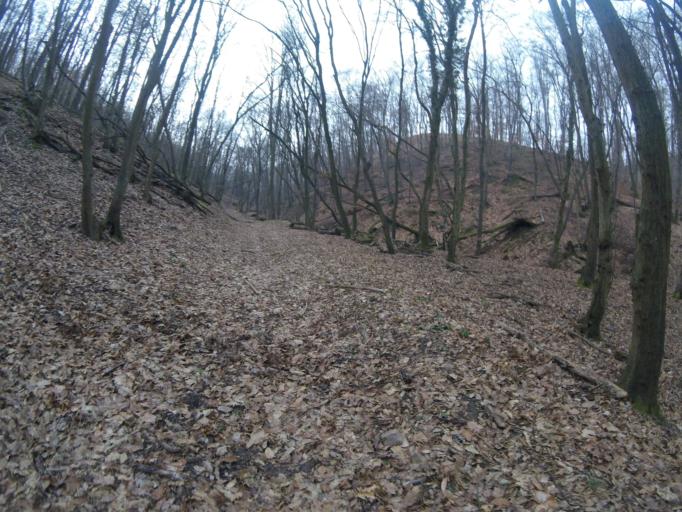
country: HU
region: Baranya
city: Mecseknadasd
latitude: 46.1450
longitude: 18.5155
